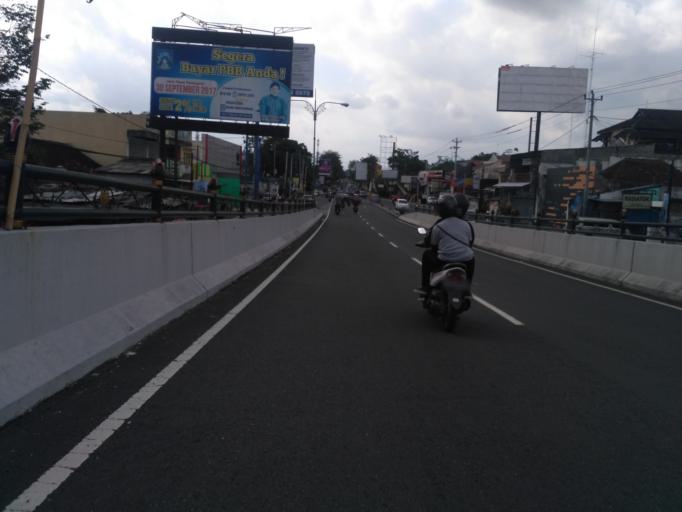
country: ID
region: Daerah Istimewa Yogyakarta
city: Melati
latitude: -7.7465
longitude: 110.3625
